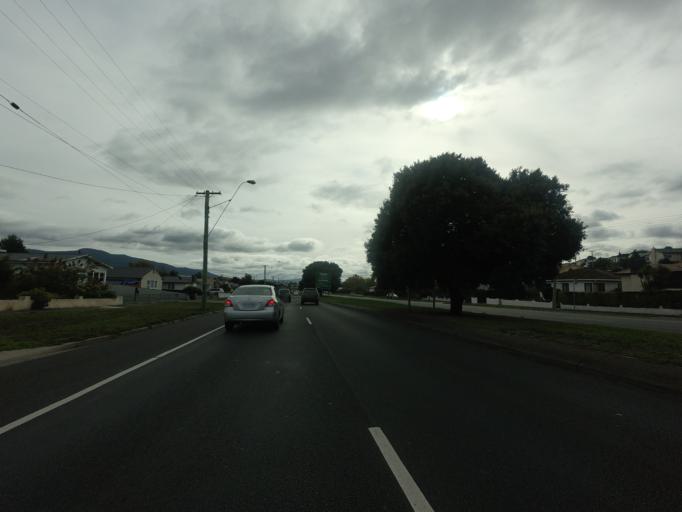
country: AU
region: Tasmania
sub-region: Glenorchy
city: Moonah
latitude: -42.8411
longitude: 147.3054
